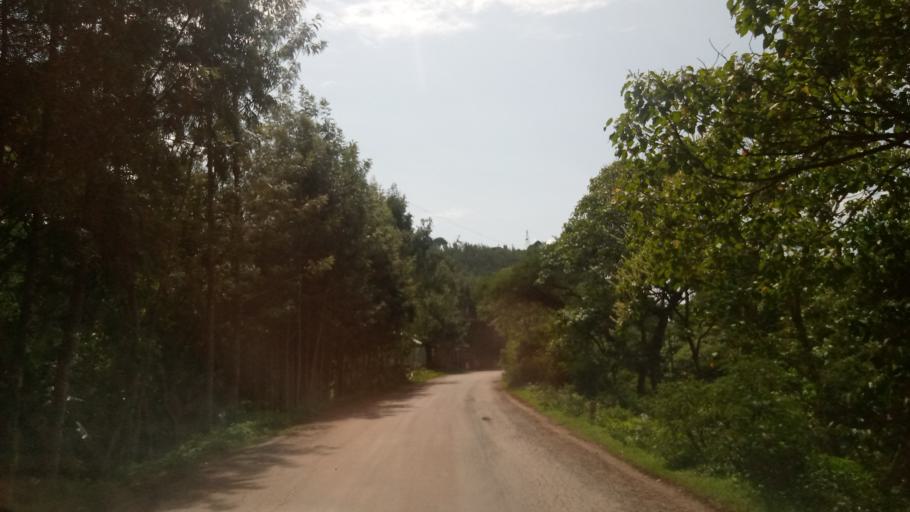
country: ET
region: Oromiya
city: Agaro
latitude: 7.9222
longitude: 36.5172
